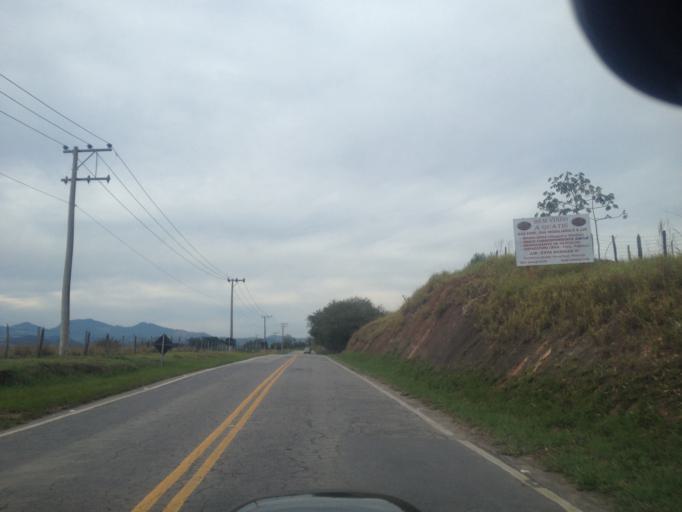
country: BR
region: Rio de Janeiro
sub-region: Porto Real
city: Porto Real
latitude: -22.4451
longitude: -44.2939
